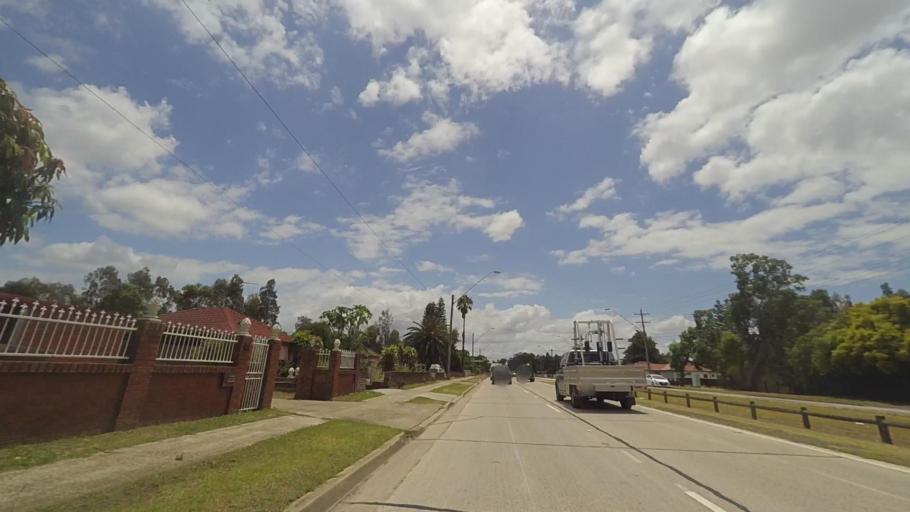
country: AU
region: New South Wales
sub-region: Fairfield
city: Fairfield Heights
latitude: -33.8786
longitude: 150.9248
